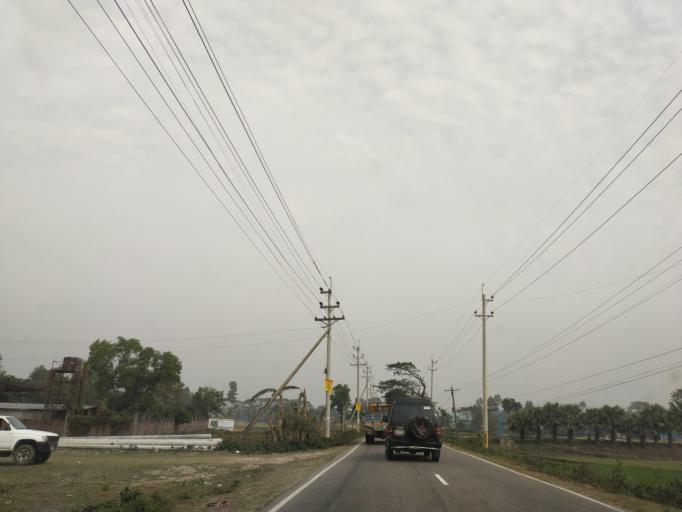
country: BD
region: Dhaka
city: Narsingdi
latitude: 23.9930
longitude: 90.7368
